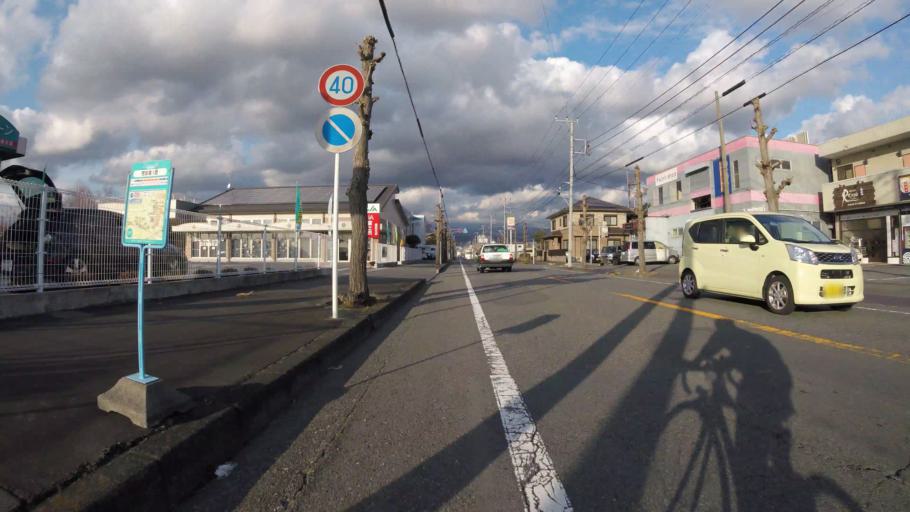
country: JP
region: Shizuoka
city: Fuji
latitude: 35.1537
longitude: 138.6831
